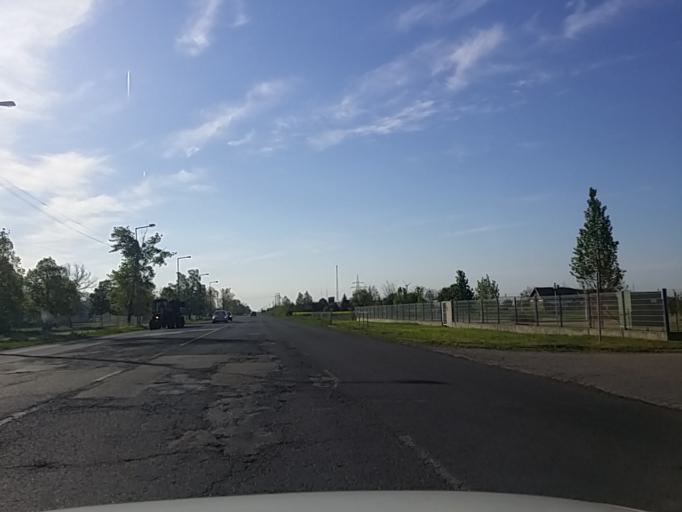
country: HU
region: Jasz-Nagykun-Szolnok
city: Torokszentmiklos
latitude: 47.1640
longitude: 20.4312
